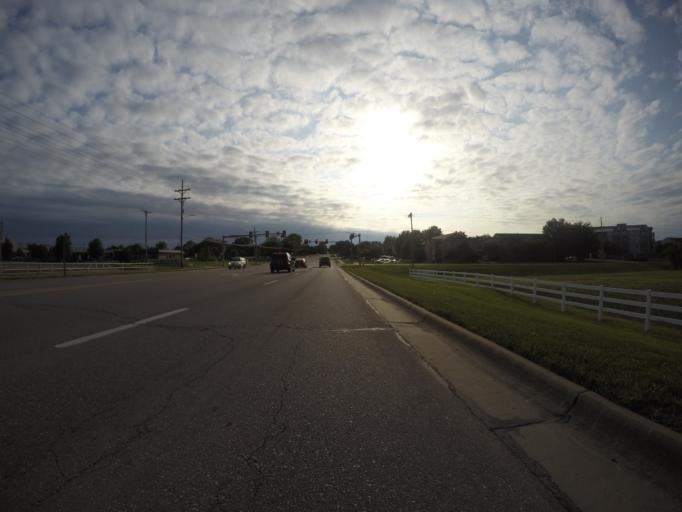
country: US
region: Kansas
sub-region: Riley County
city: Manhattan
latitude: 39.2041
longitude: -96.5973
